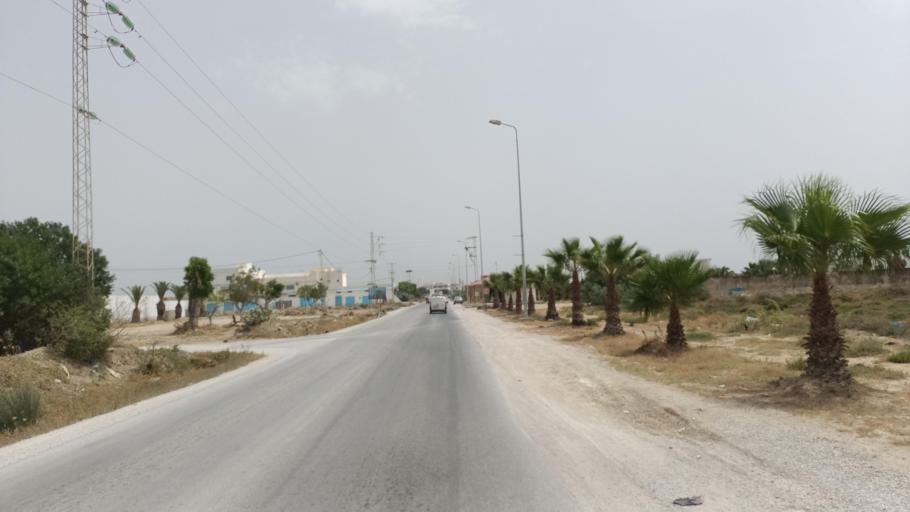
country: TN
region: Nabul
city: Manzil Bu Zalafah
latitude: 36.7113
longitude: 10.4819
